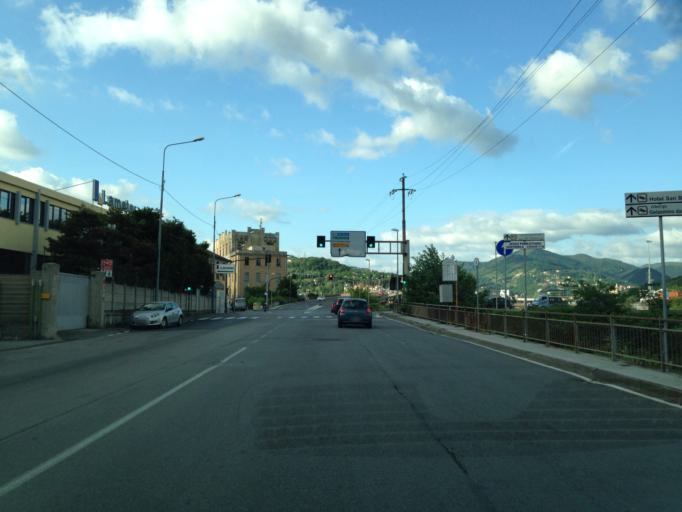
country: IT
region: Liguria
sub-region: Provincia di Genova
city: Manesseno
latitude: 44.4642
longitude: 8.8974
